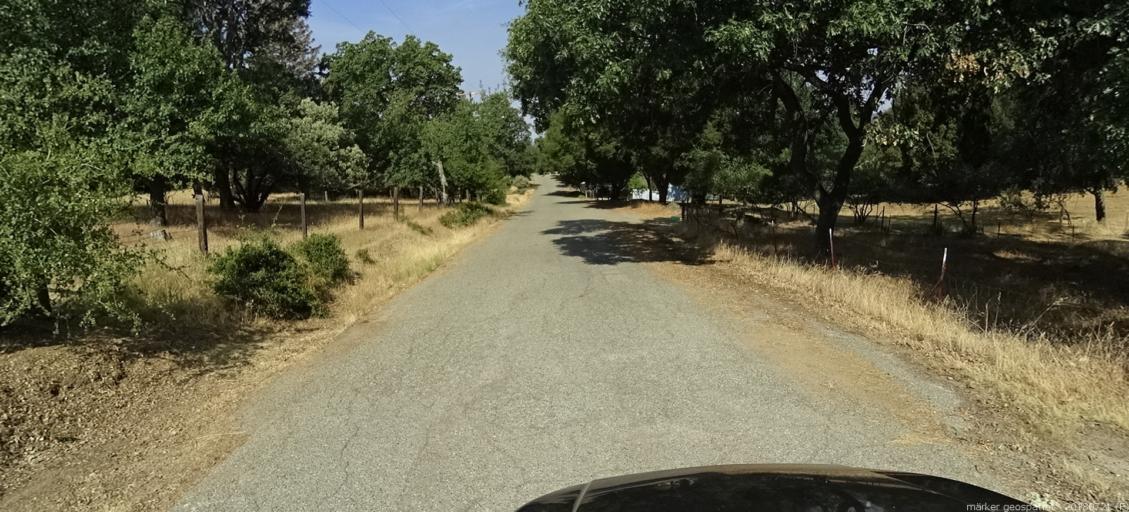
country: US
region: California
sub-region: Fresno County
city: Auberry
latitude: 37.2213
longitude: -119.5247
